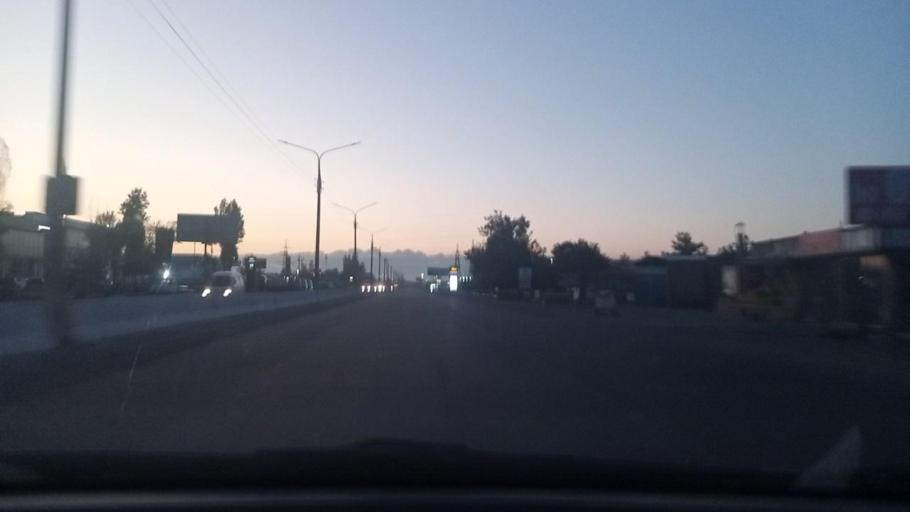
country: UZ
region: Toshkent Shahri
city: Tashkent
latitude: 41.2439
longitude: 69.2274
